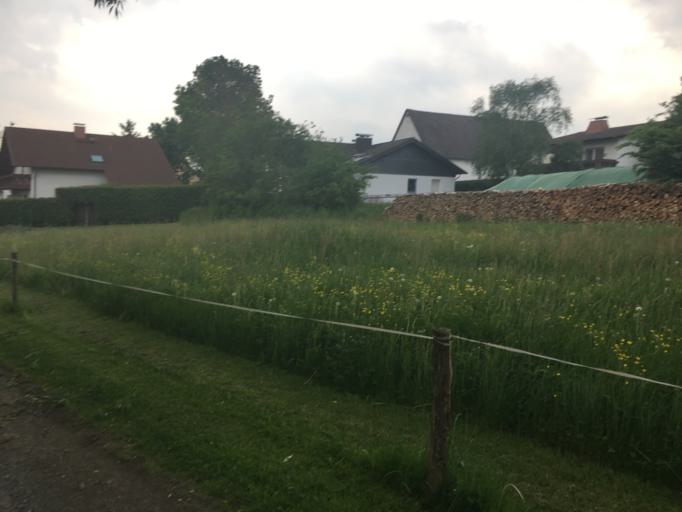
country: DE
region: Hesse
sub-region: Regierungsbezirk Darmstadt
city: Wehrheim
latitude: 50.3055
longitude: 8.5755
